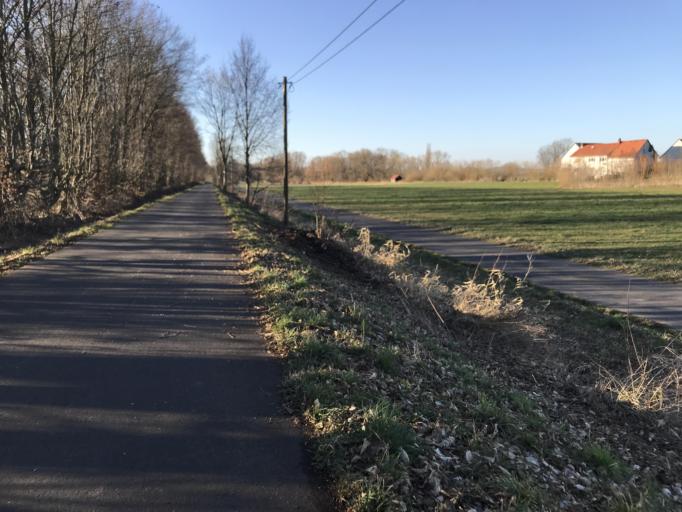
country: DE
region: Hesse
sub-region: Regierungsbezirk Kassel
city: Schrecksbach
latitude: 50.8798
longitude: 9.2631
